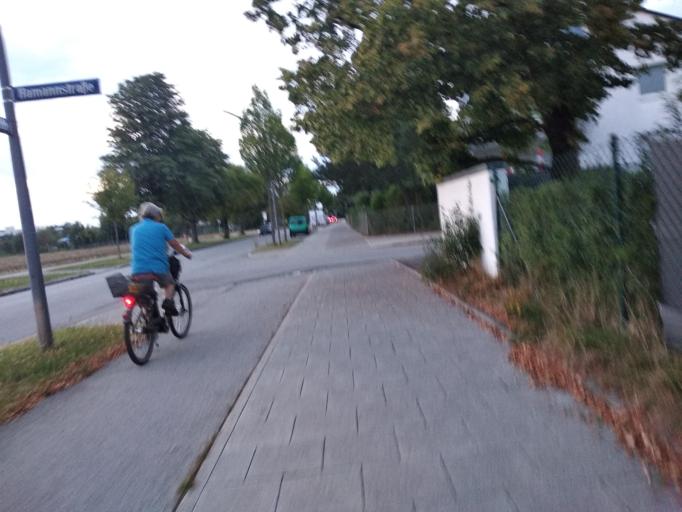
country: DE
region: Bavaria
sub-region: Upper Bavaria
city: Neubiberg
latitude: 48.0888
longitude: 11.6617
